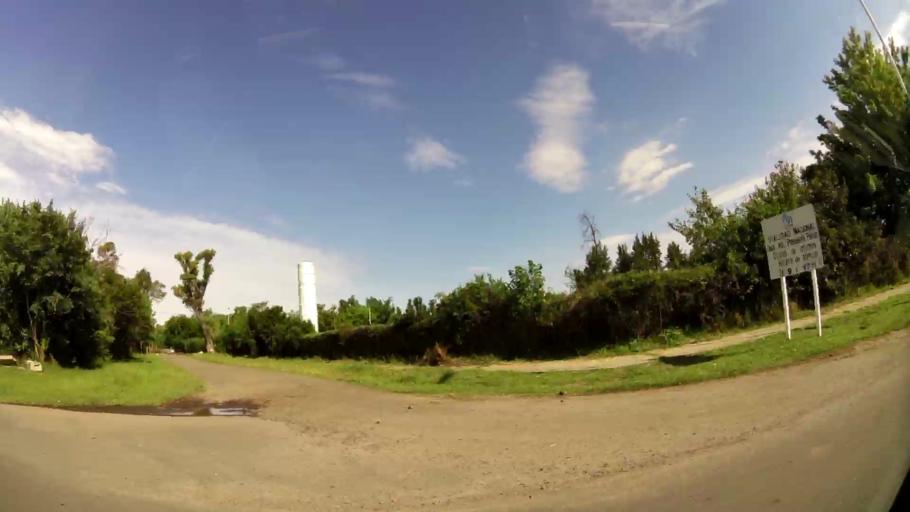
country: AR
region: Buenos Aires
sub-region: Partido de Merlo
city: Merlo
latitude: -34.6577
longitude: -58.7531
